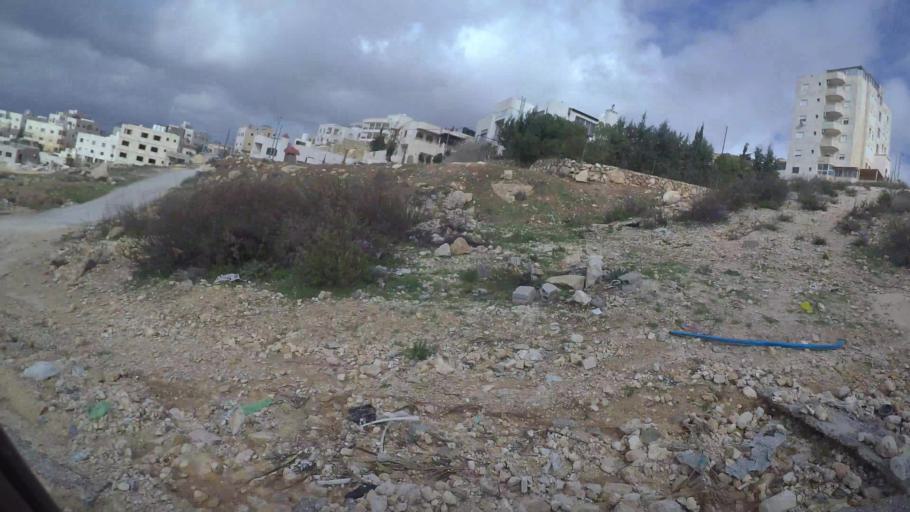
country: JO
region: Amman
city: Al Jubayhah
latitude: 32.0605
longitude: 35.8668
